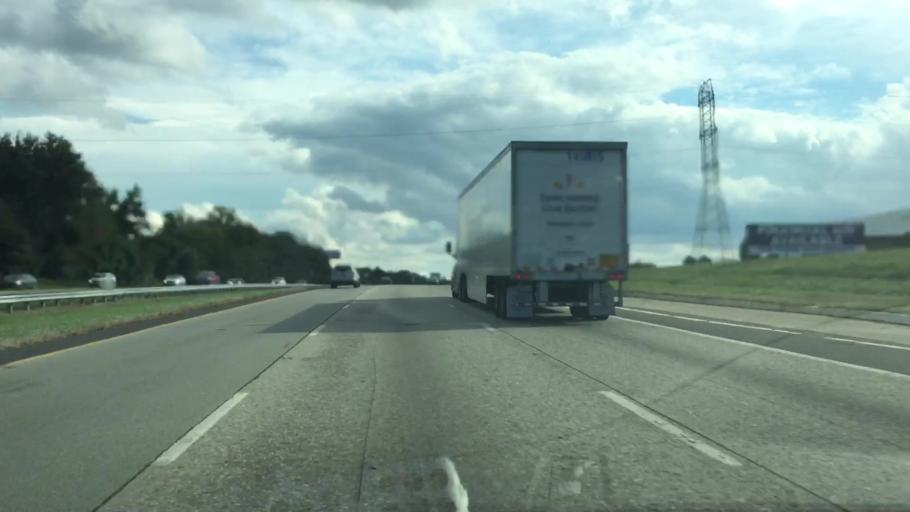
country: US
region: New Jersey
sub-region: Camden County
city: Blackwood
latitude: 39.8093
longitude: -75.0601
